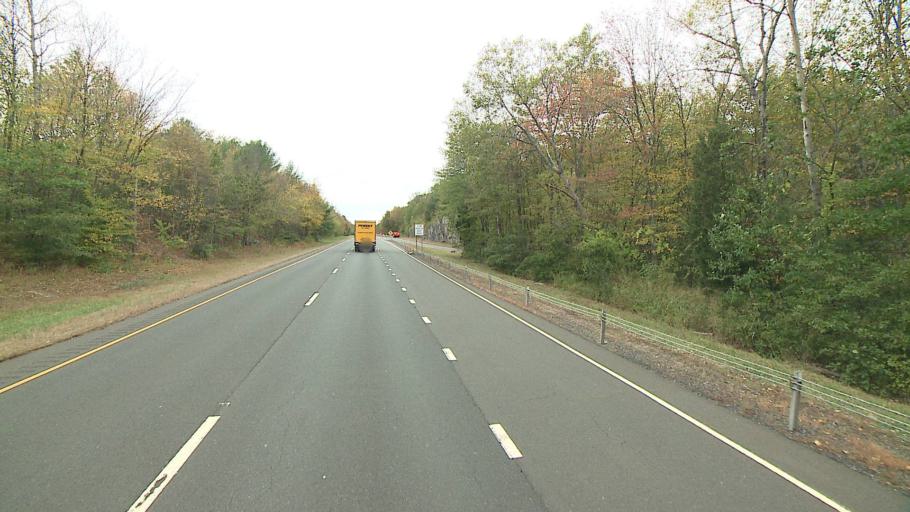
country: US
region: Connecticut
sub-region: Middlesex County
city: Higganum
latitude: 41.4571
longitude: -72.5284
